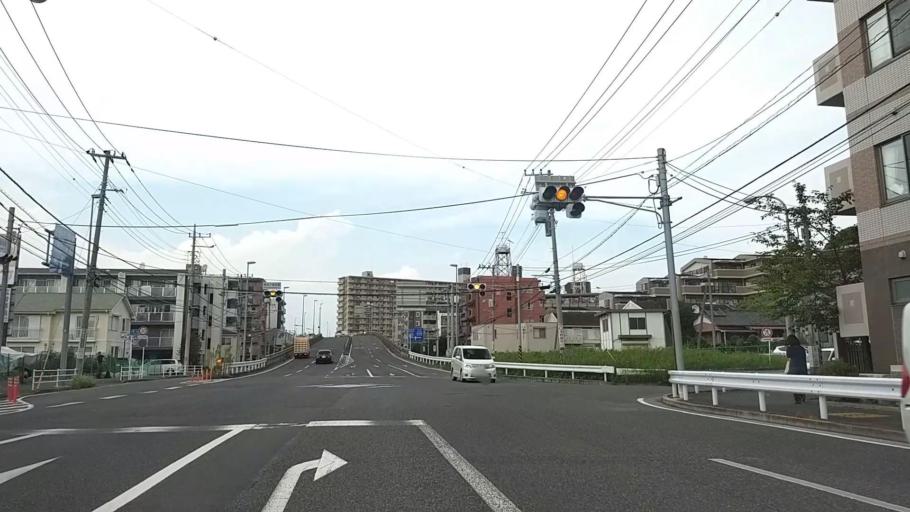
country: JP
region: Kanagawa
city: Yokohama
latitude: 35.5082
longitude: 139.5642
